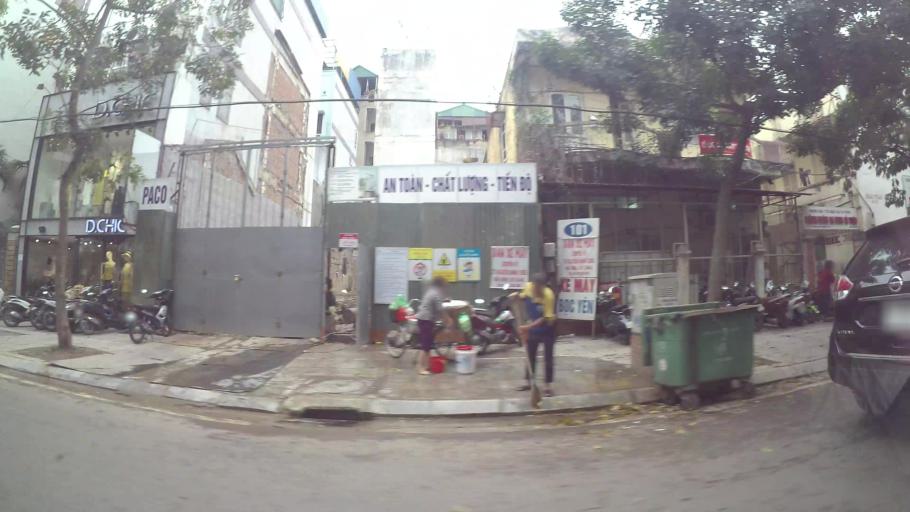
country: VN
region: Ha Noi
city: Hai BaTrung
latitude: 21.0163
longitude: 105.8492
